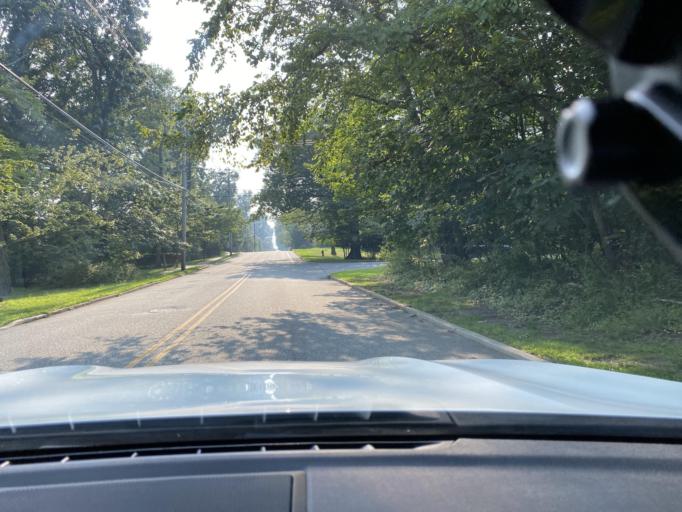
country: US
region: New York
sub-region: Rockland County
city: Airmont
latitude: 41.0896
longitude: -74.1272
